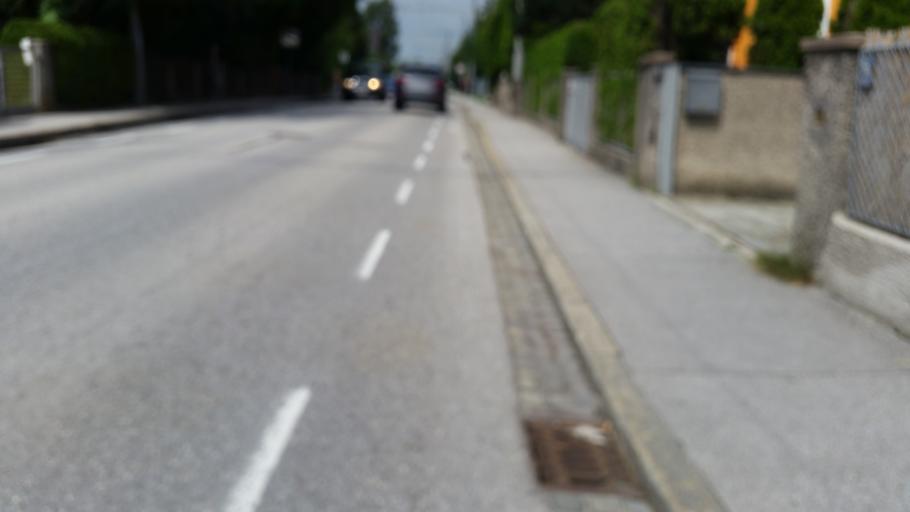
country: AT
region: Salzburg
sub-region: Politischer Bezirk Salzburg-Umgebung
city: Bergheim
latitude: 47.8121
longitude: 13.0067
